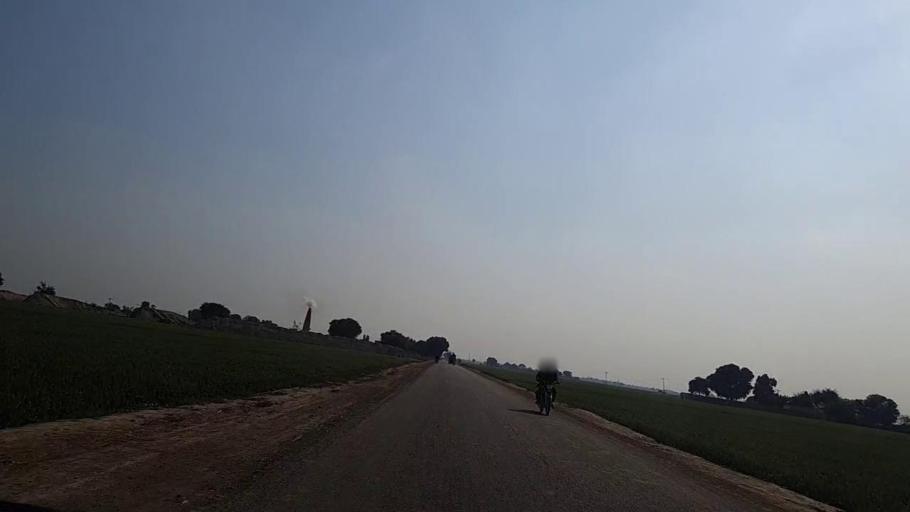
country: PK
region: Sindh
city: Sakrand
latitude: 26.1016
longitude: 68.2907
